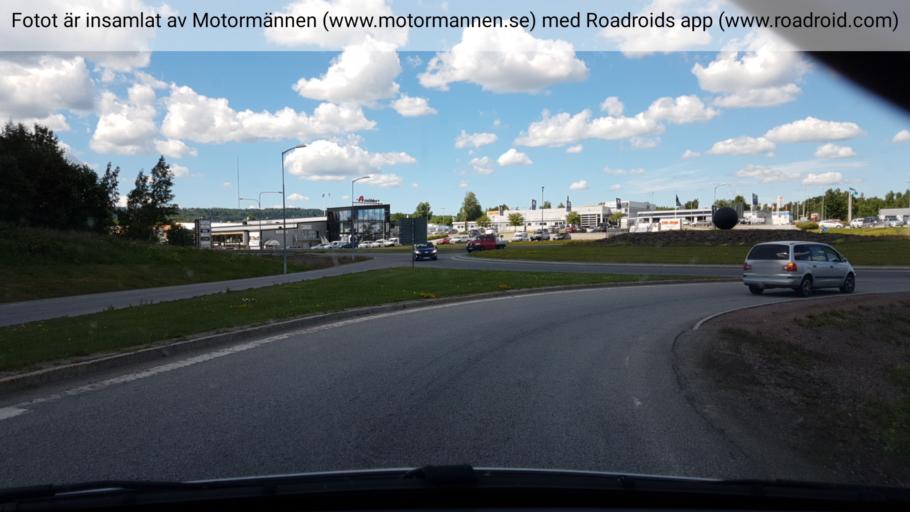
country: SE
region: Vaestra Goetaland
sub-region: Skovde Kommun
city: Skoevde
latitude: 58.3932
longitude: 13.8726
